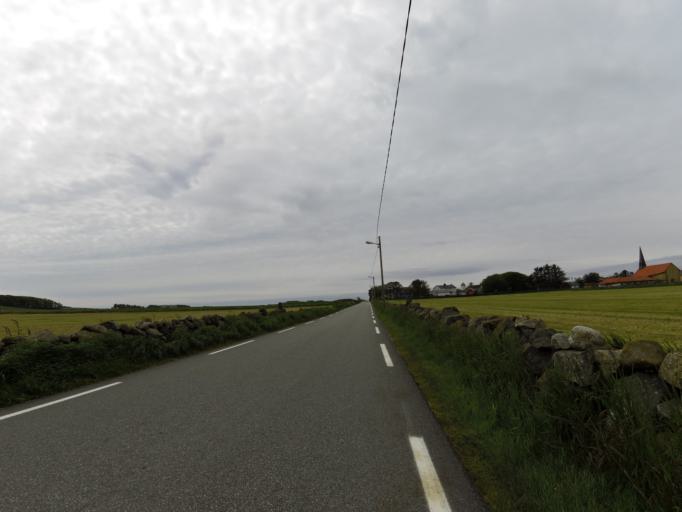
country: NO
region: Rogaland
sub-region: Ha
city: Naerbo
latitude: 58.6809
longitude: 5.5645
